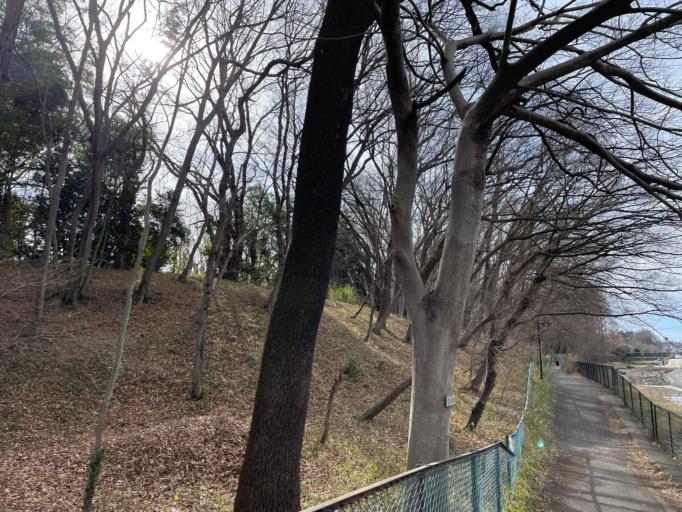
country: JP
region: Saitama
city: Tokorozawa
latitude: 35.7814
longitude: 139.5078
